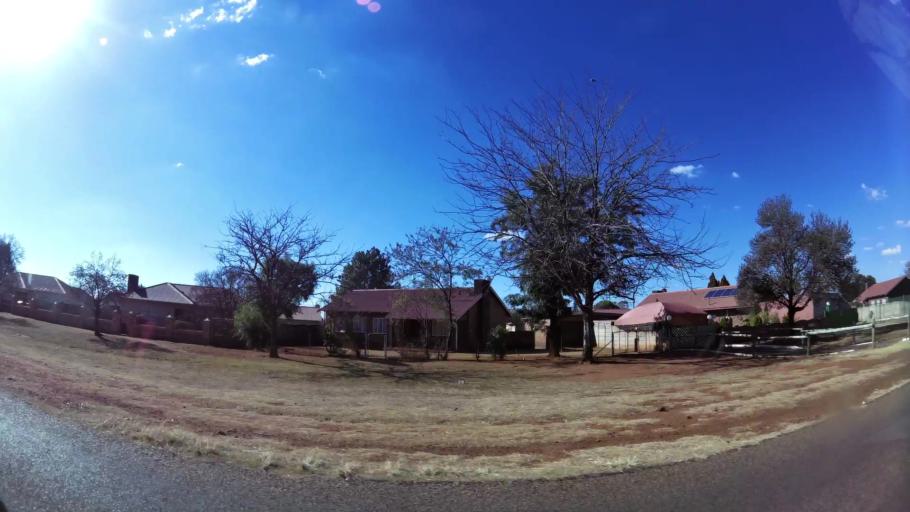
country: ZA
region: Gauteng
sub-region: West Rand District Municipality
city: Carletonville
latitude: -26.3609
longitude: 27.3788
